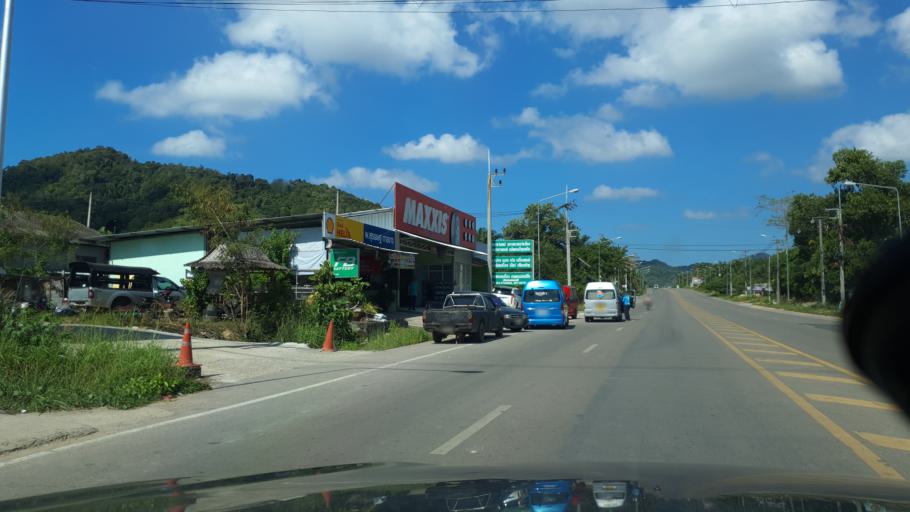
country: TH
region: Phangnga
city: Ban Ao Nang
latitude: 8.0354
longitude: 98.8572
